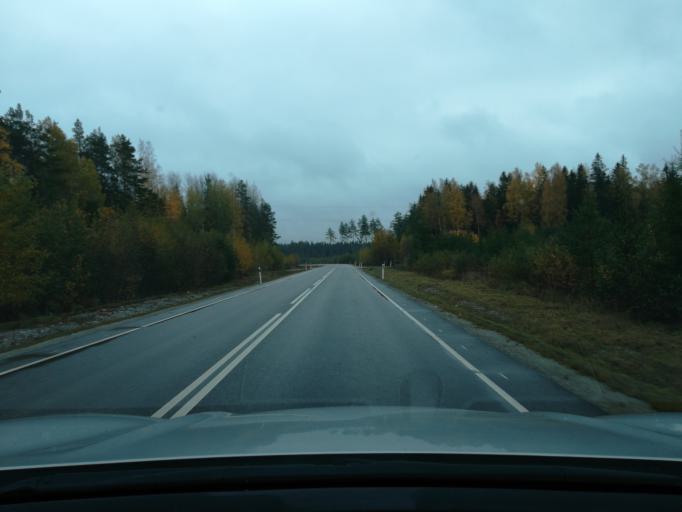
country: EE
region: Ida-Virumaa
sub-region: Johvi vald
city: Johvi
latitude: 59.3022
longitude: 27.4678
